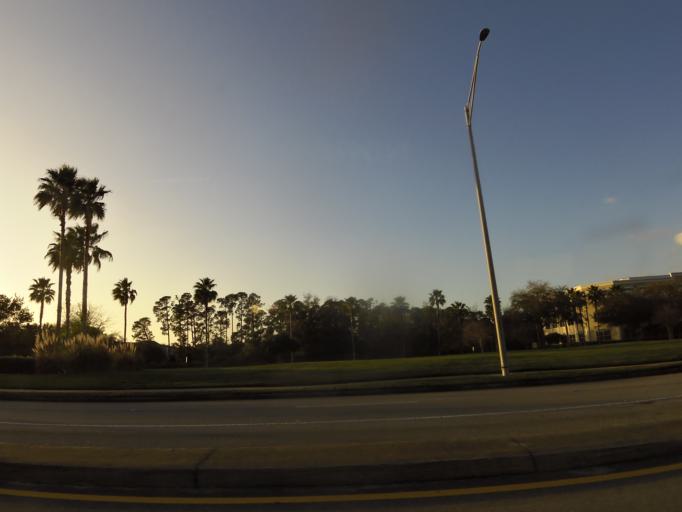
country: US
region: Florida
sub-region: Duval County
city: Jacksonville Beach
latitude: 30.2582
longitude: -81.4625
